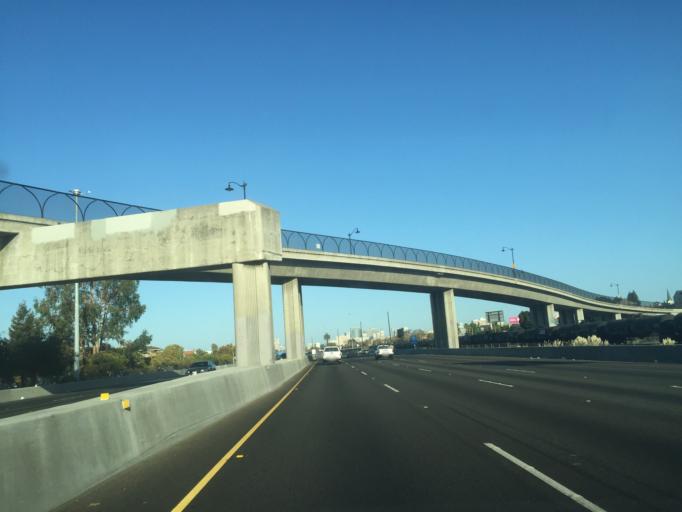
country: US
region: California
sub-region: Alameda County
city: Alameda
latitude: 37.7856
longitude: -122.2439
